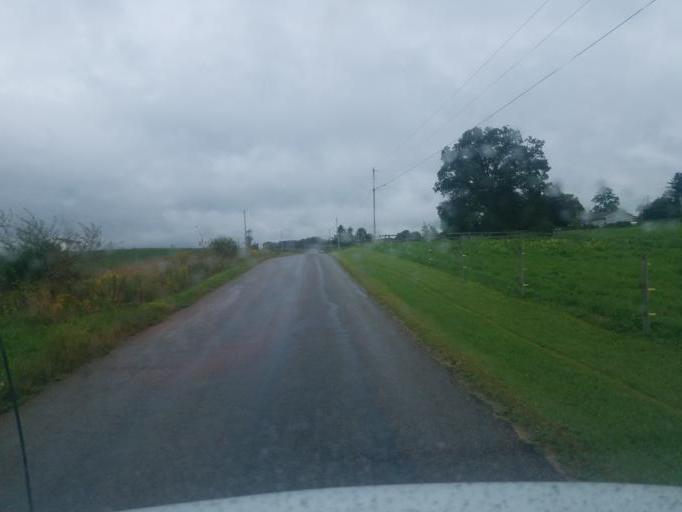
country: US
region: Ohio
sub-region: Wayne County
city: West Salem
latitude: 40.9229
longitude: -82.1187
